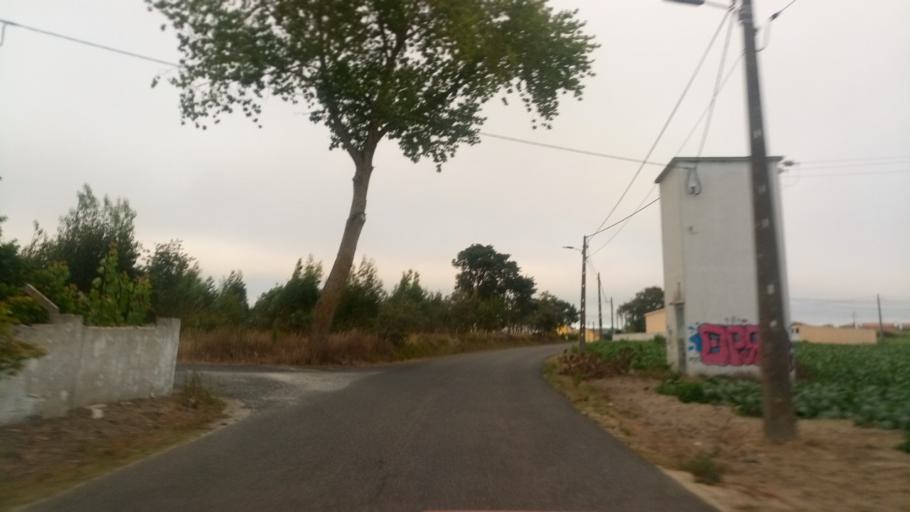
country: PT
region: Leiria
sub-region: Caldas da Rainha
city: Caldas da Rainha
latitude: 39.4202
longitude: -9.1471
